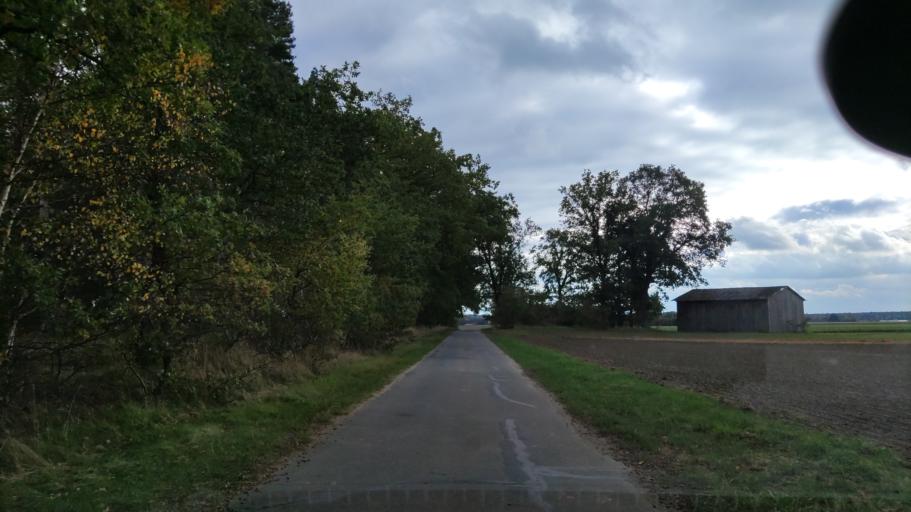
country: DE
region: Lower Saxony
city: Vastorf
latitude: 53.1574
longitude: 10.5347
